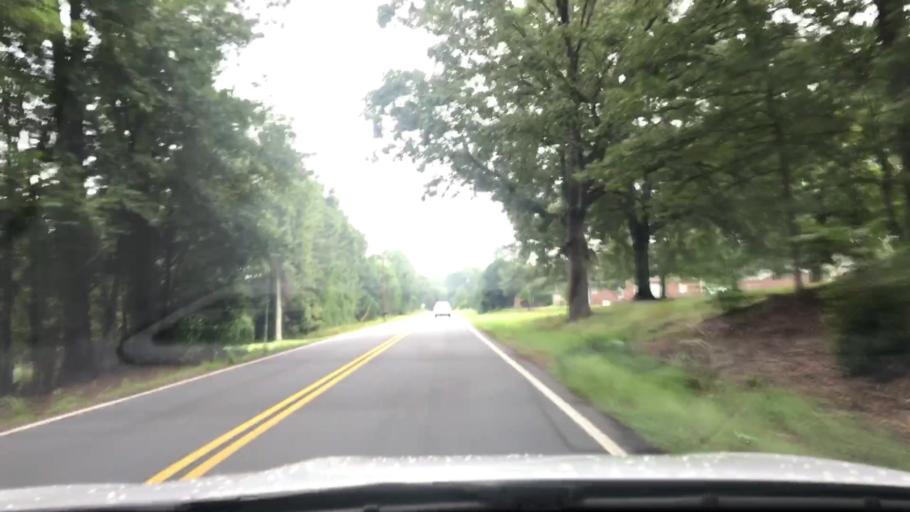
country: US
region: South Carolina
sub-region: Spartanburg County
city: Roebuck
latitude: 34.8275
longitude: -81.9577
